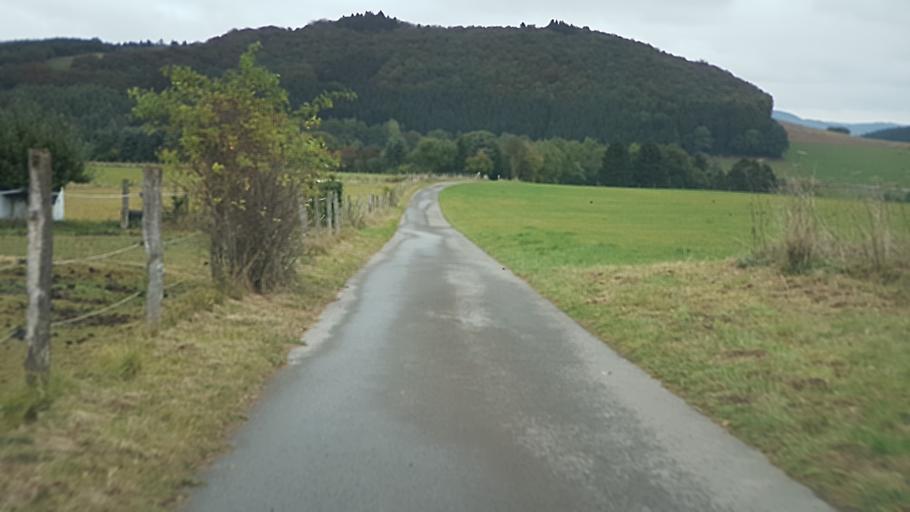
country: DE
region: North Rhine-Westphalia
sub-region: Regierungsbezirk Arnsberg
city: Herscheid
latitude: 51.1581
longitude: 7.7661
